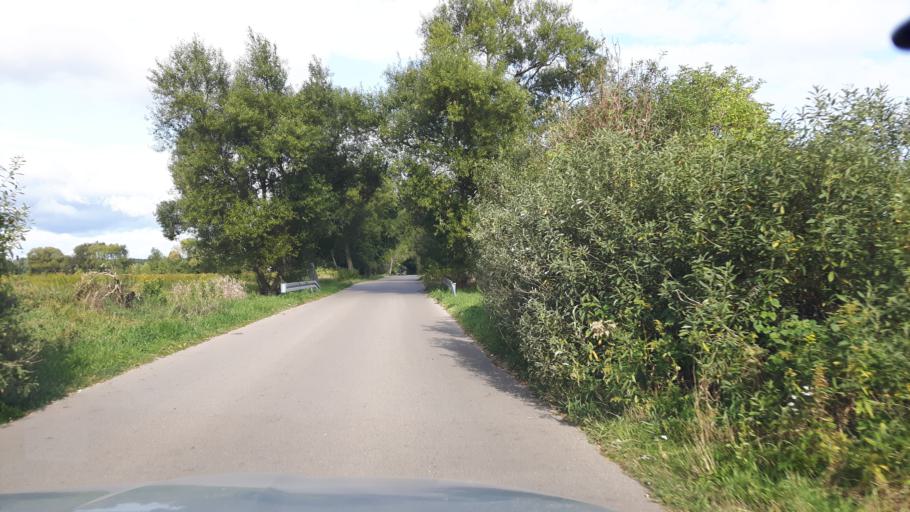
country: PL
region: Masovian Voivodeship
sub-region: Powiat wolominski
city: Marki
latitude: 52.3333
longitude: 21.0725
